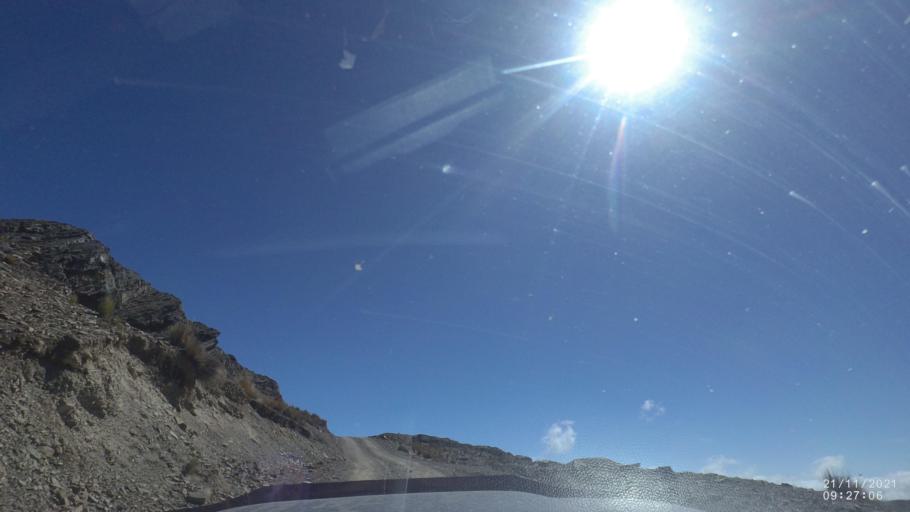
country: BO
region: Cochabamba
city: Cochabamba
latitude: -17.0850
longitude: -66.2513
